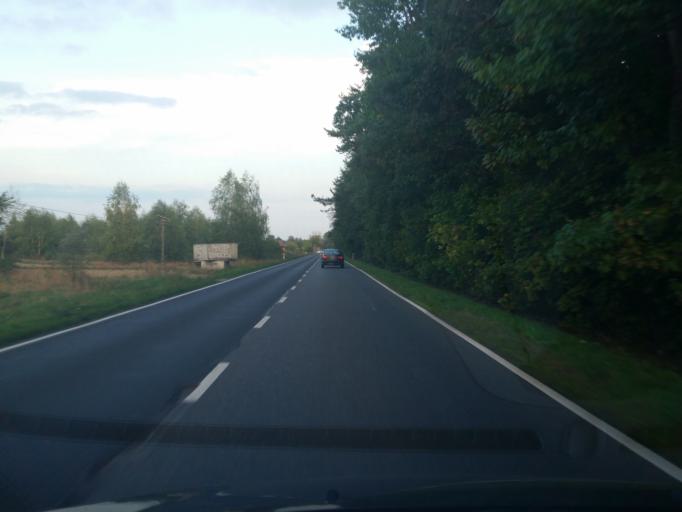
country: PL
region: Masovian Voivodeship
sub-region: Powiat nowodworski
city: Zakroczym
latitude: 52.3946
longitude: 20.6526
